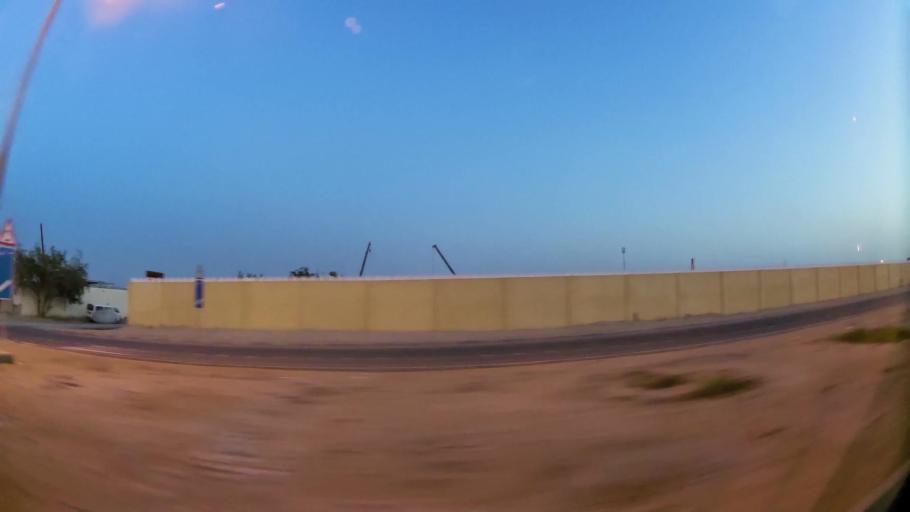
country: QA
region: Baladiyat ar Rayyan
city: Ar Rayyan
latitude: 25.3035
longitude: 51.4526
